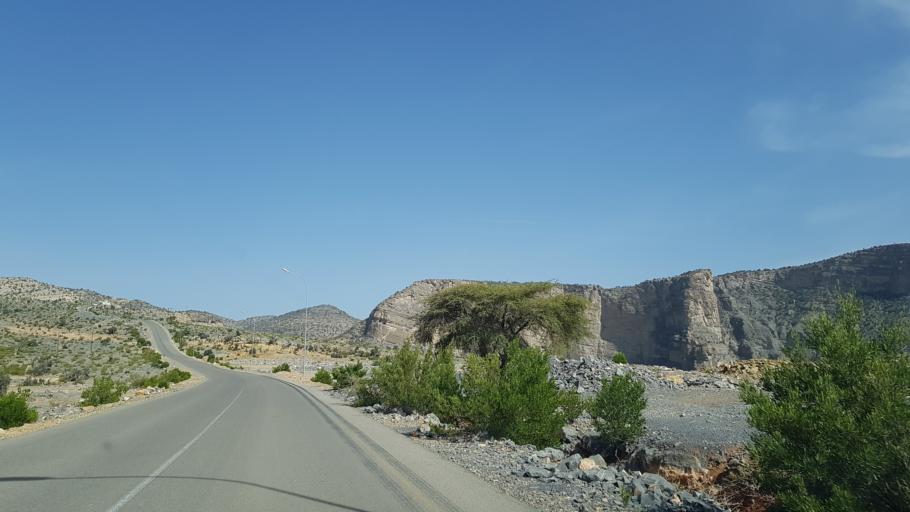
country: OM
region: Al Batinah
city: Bayt al `Awabi
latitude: 23.1376
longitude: 57.5447
